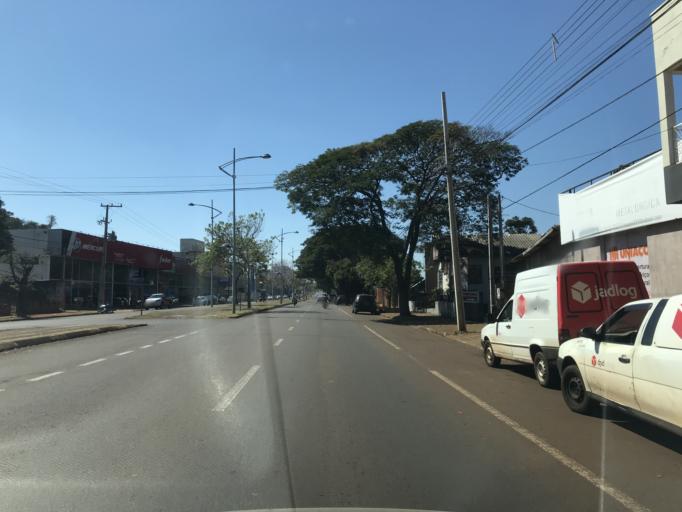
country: BR
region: Parana
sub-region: Toledo
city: Toledo
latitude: -24.7262
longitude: -53.7319
